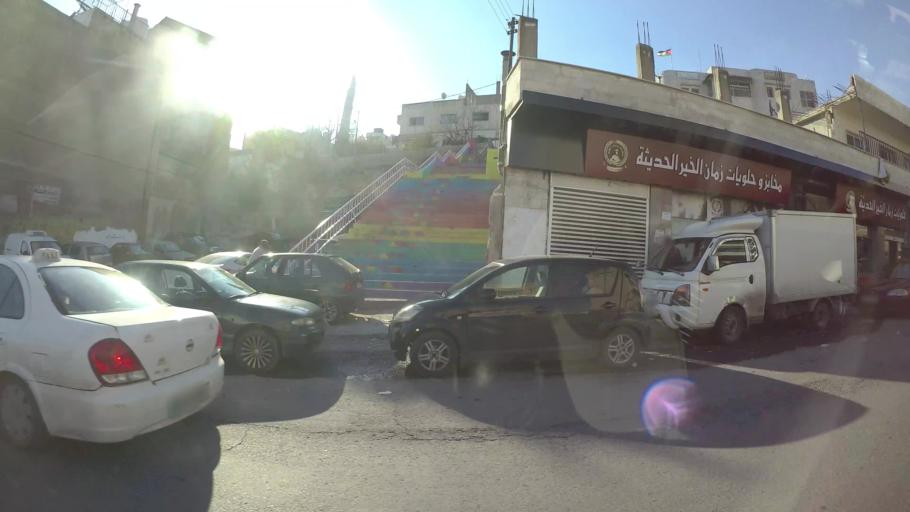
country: JO
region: Amman
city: Amman
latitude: 31.9678
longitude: 35.9606
